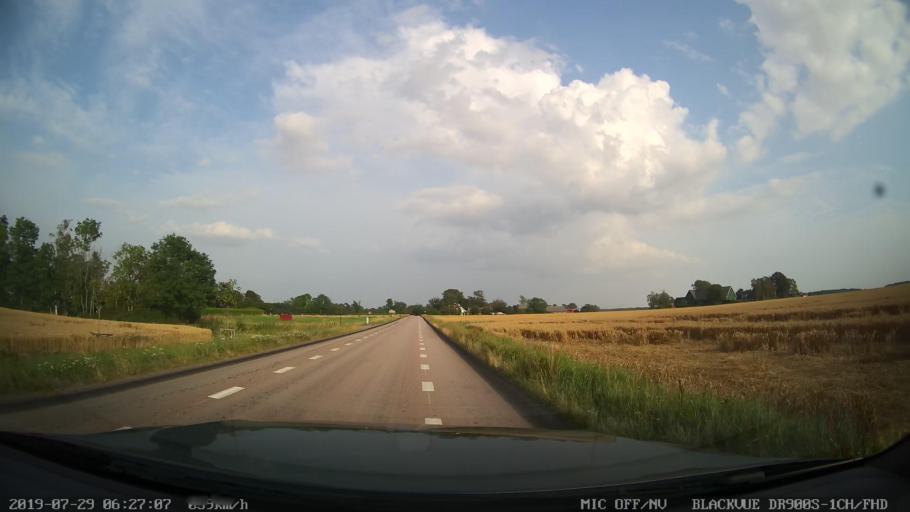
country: SE
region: Skane
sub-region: Helsingborg
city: Odakra
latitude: 56.1087
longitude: 12.7109
